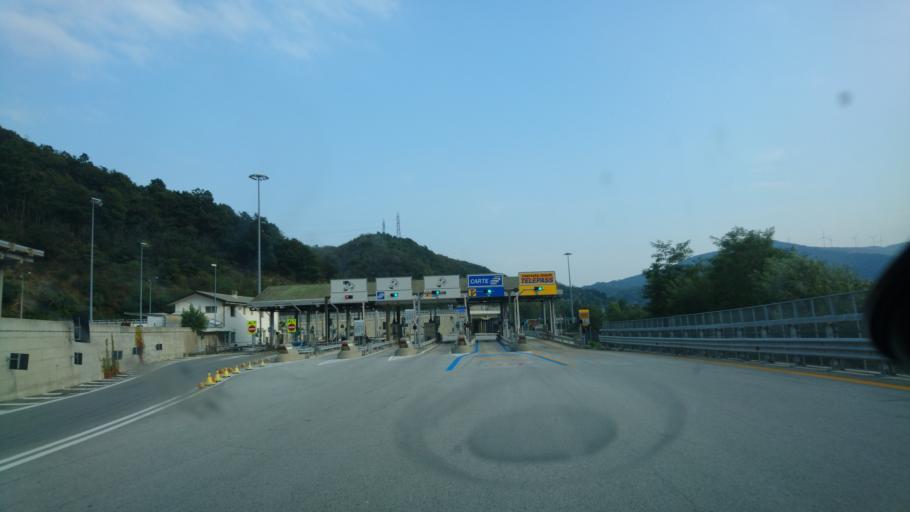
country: IT
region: Liguria
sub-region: Provincia di Savona
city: Altare
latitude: 44.3456
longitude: 8.3220
